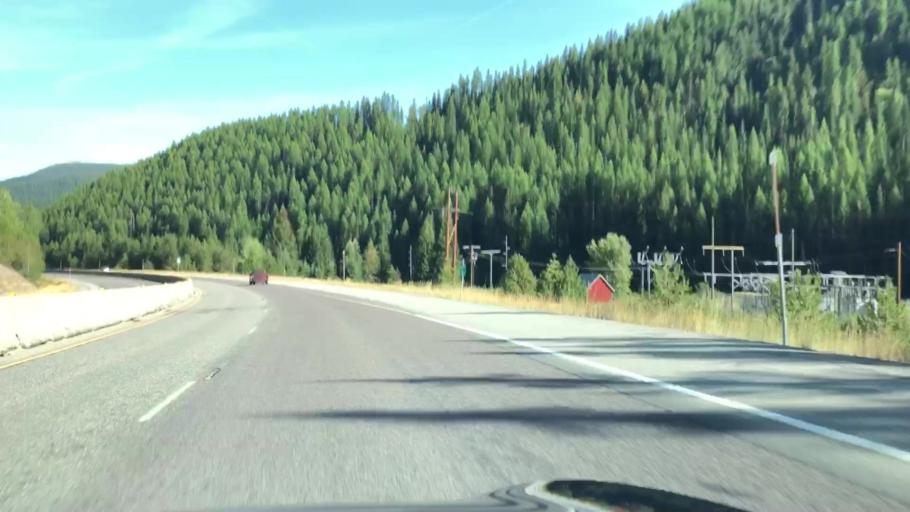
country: US
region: Montana
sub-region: Sanders County
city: Thompson Falls
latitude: 47.4195
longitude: -115.6019
